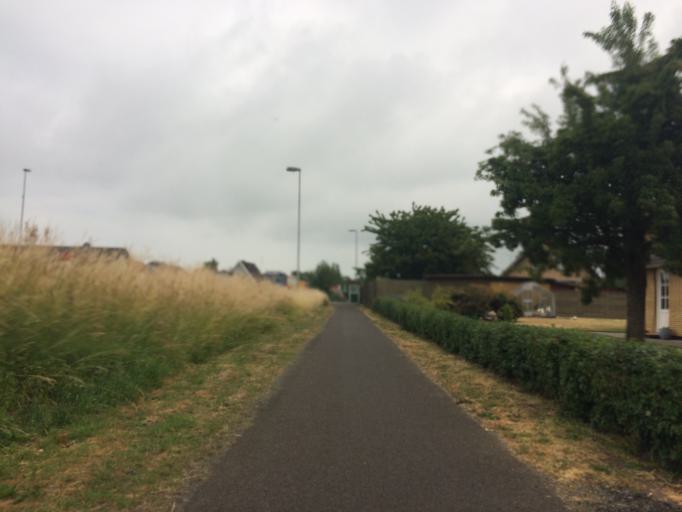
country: DK
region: Capital Region
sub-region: Bornholm Kommune
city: Ronne
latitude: 55.1012
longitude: 14.7203
